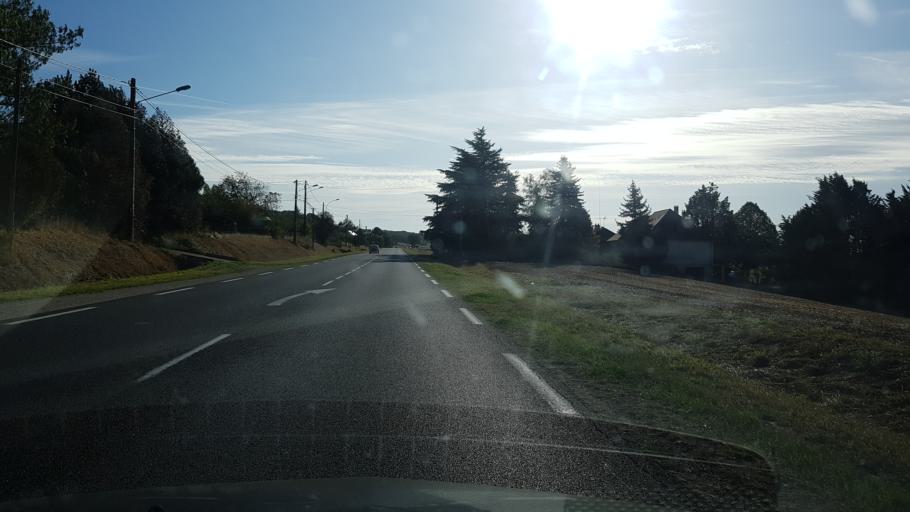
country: FR
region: Centre
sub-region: Departement du Loiret
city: Saint-Brisson-sur-Loire
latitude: 47.6697
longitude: 2.6843
